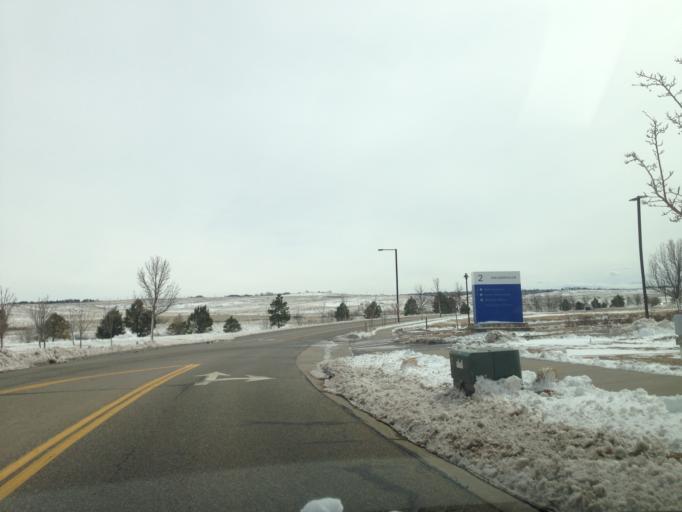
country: US
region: Colorado
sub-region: Boulder County
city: Lafayette
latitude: 39.9716
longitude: -105.0837
